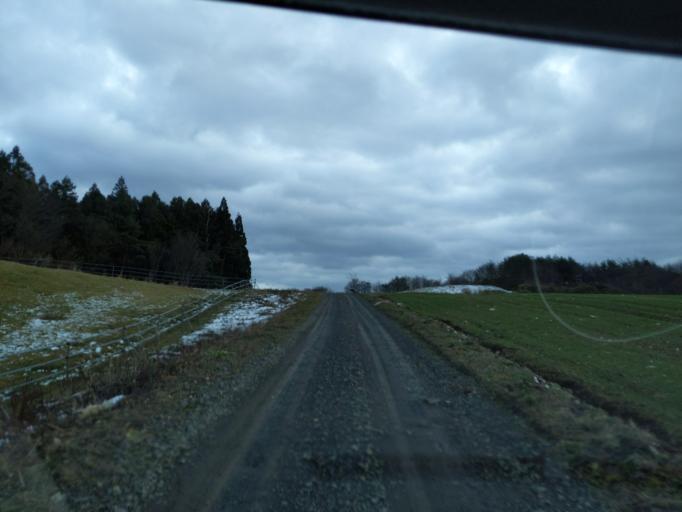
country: JP
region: Iwate
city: Ichinoseki
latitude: 38.9800
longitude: 141.0137
